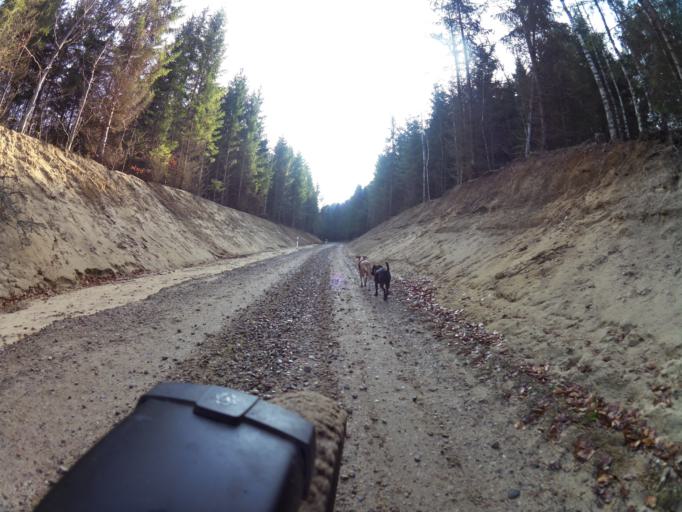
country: PL
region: West Pomeranian Voivodeship
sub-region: Powiat koszalinski
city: Polanow
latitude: 54.1790
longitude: 16.7212
